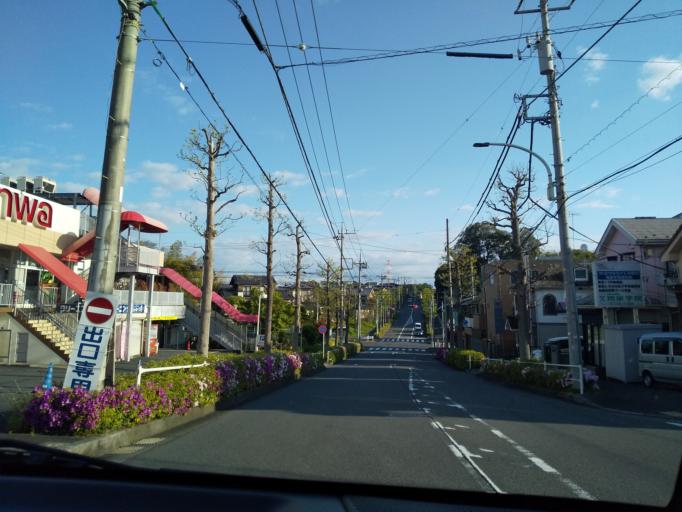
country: JP
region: Tokyo
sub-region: Machida-shi
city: Machida
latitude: 35.5758
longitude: 139.4552
